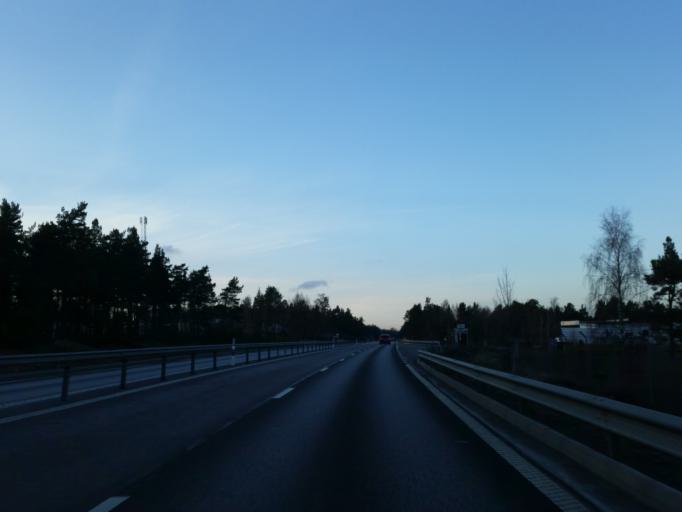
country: SE
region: Kalmar
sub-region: Oskarshamns Kommun
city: Oskarshamn
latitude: 57.3816
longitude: 16.4822
